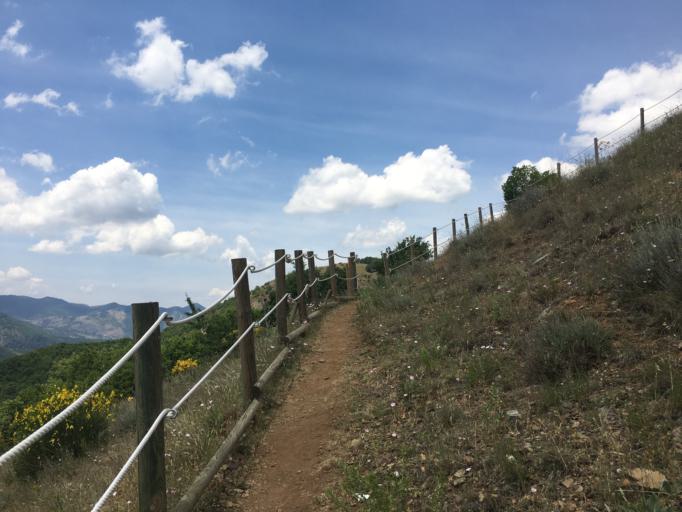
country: IT
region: Basilicate
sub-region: Provincia di Potenza
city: Sasso di Castalda
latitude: 40.4921
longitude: 15.6726
